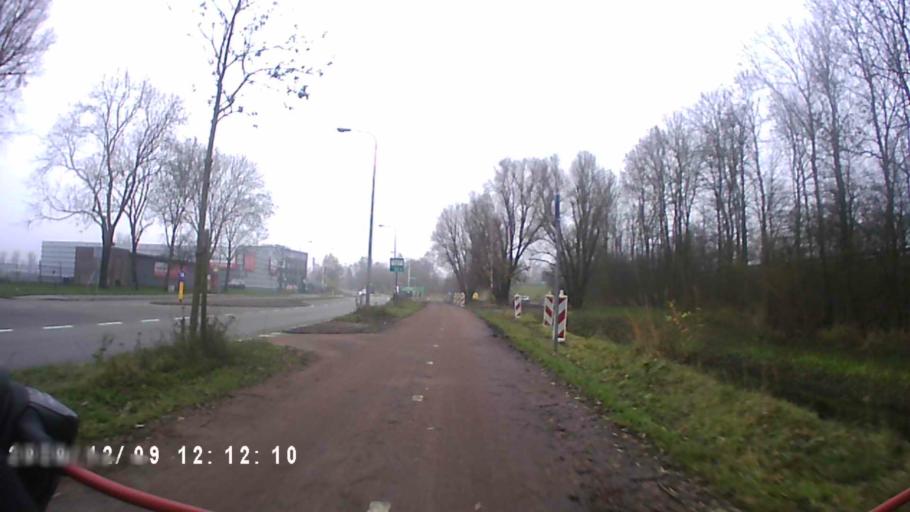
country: NL
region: Groningen
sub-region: Gemeente Groningen
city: Oosterpark
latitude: 53.2045
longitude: 6.6009
